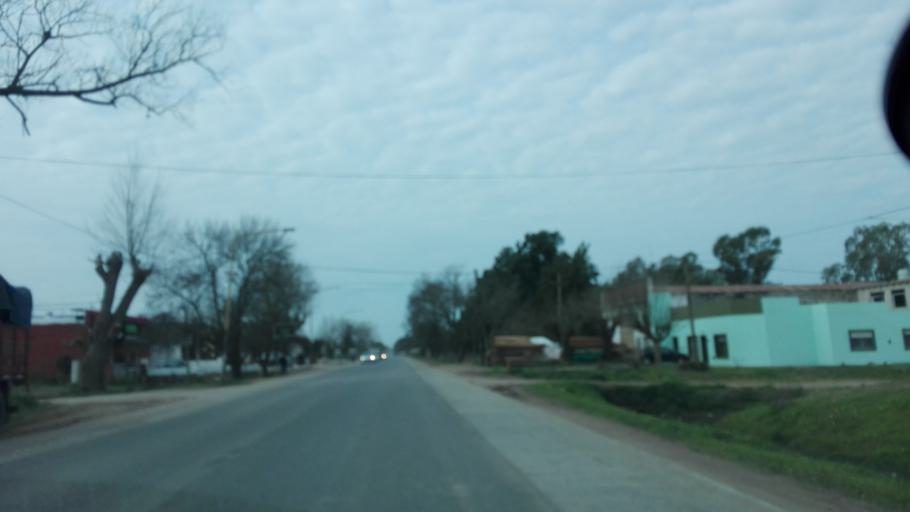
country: AR
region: Buenos Aires
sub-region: Partido de Chascomus
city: Chascomus
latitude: -35.5756
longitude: -57.9968
